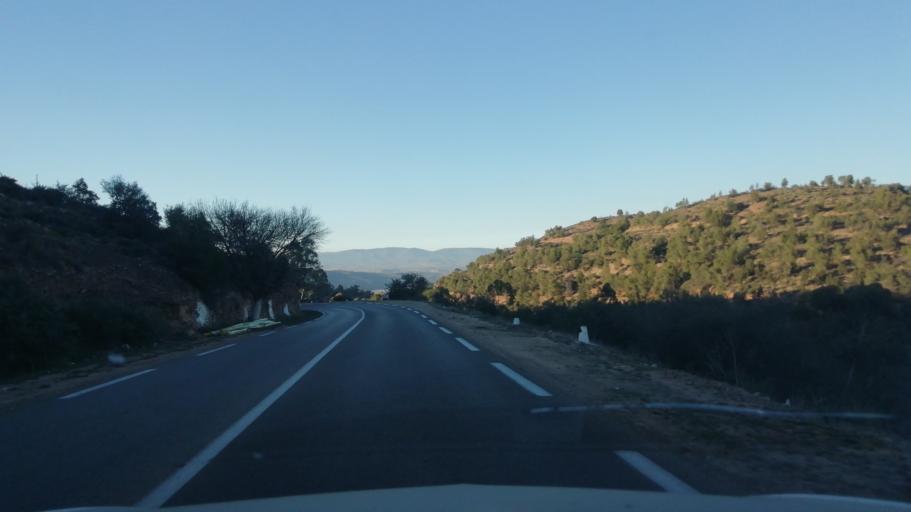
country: DZ
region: Tlemcen
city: Beni Mester
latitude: 34.8152
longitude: -1.6324
